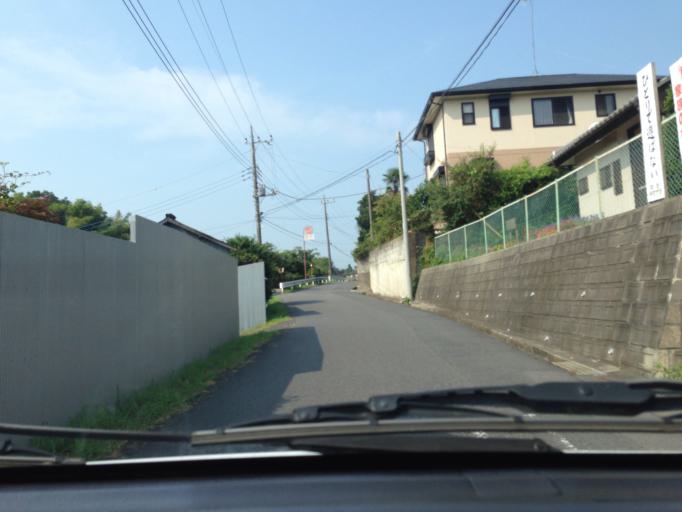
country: JP
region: Ibaraki
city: Ami
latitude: 36.0470
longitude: 140.2125
